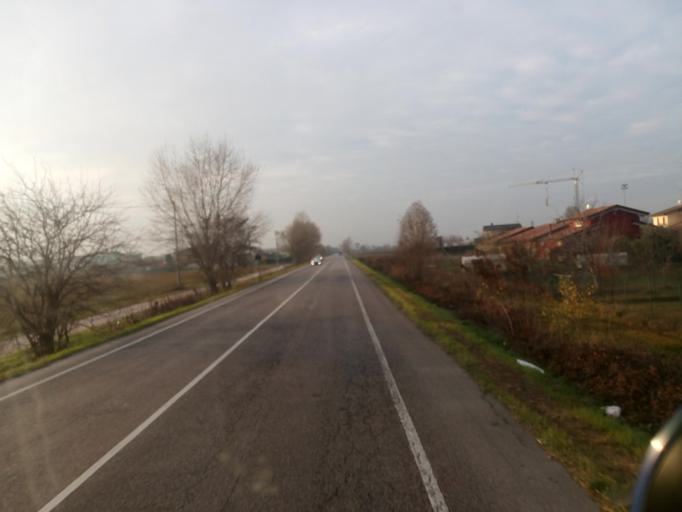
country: IT
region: Veneto
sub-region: Provincia di Verona
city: Pradelle
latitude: 45.2800
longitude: 10.8719
